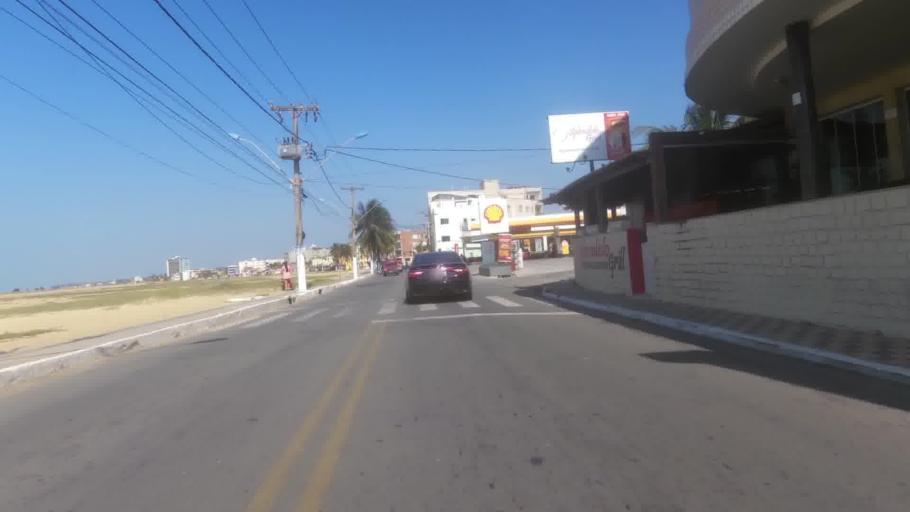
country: BR
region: Espirito Santo
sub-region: Marataizes
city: Marataizes
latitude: -21.0438
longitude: -40.8271
